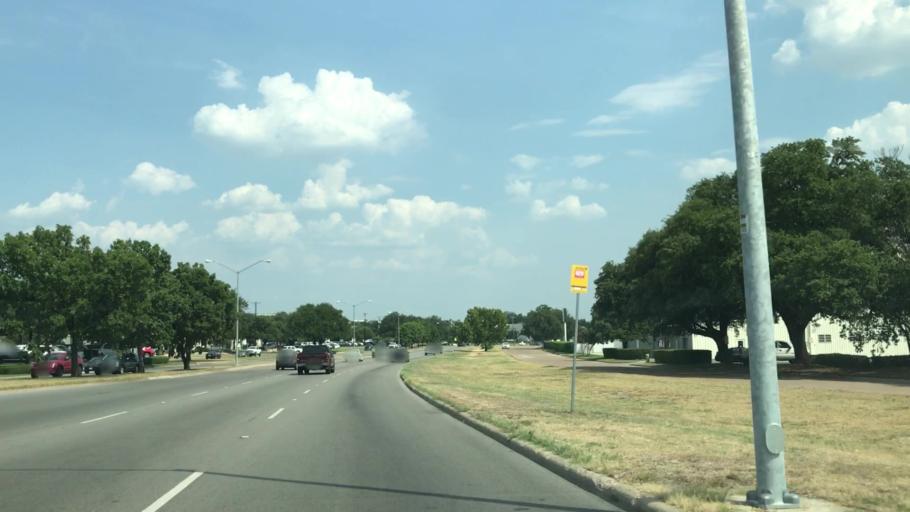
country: US
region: Texas
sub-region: Dallas County
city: University Park
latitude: 32.8473
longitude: -96.8376
